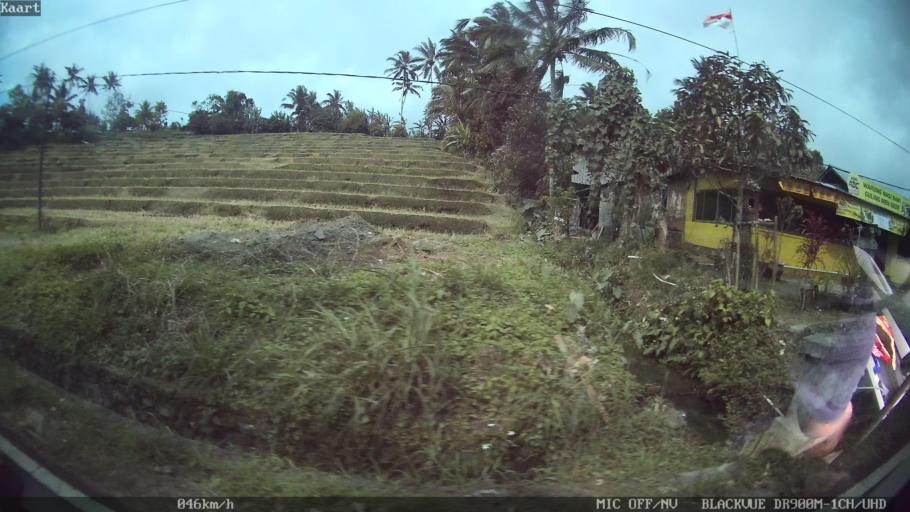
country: ID
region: Bali
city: Bantiran
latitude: -8.3137
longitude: 114.9987
